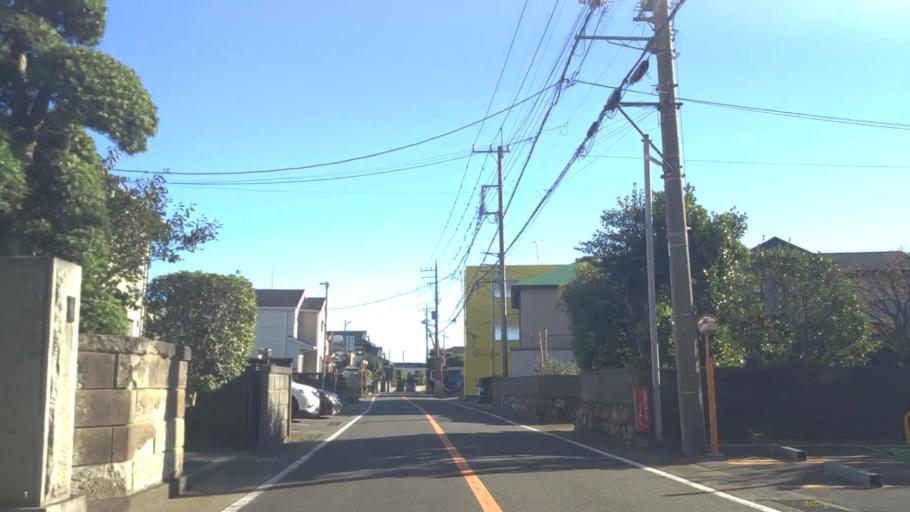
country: JP
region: Kanagawa
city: Atsugi
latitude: 35.4278
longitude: 139.3691
